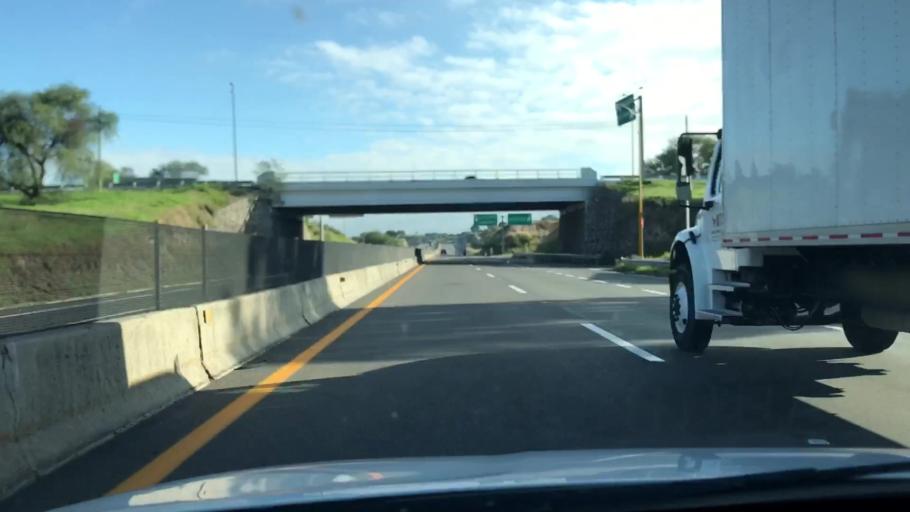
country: MX
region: Jalisco
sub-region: San Juan de los Lagos
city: Mezquitic de la Magdalena
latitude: 21.2247
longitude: -102.3136
